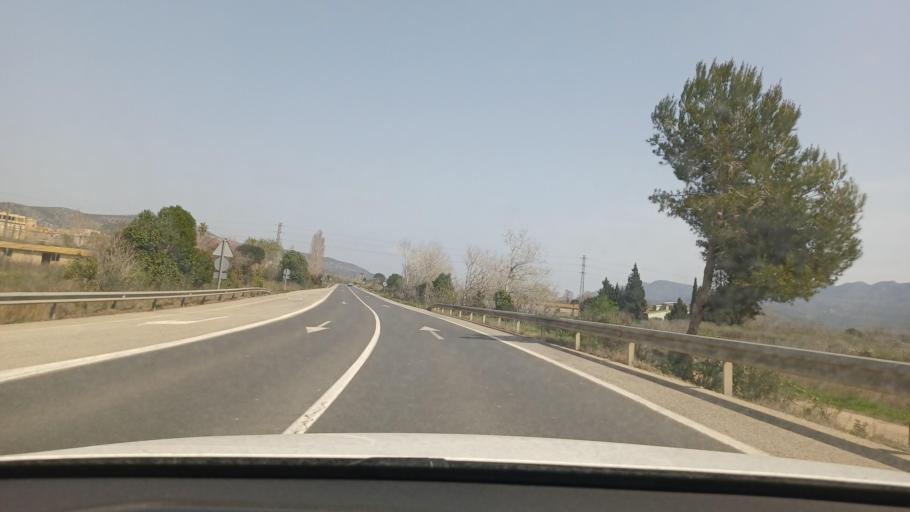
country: ES
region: Catalonia
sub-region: Provincia de Tarragona
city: Ulldecona
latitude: 40.5924
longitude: 0.4486
